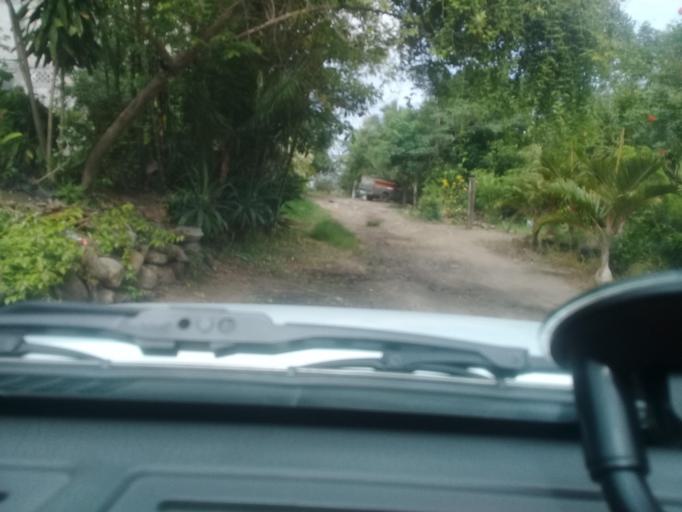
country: MX
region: Veracruz
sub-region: Paso de Ovejas
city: Tolome
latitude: 19.2703
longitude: -96.3866
